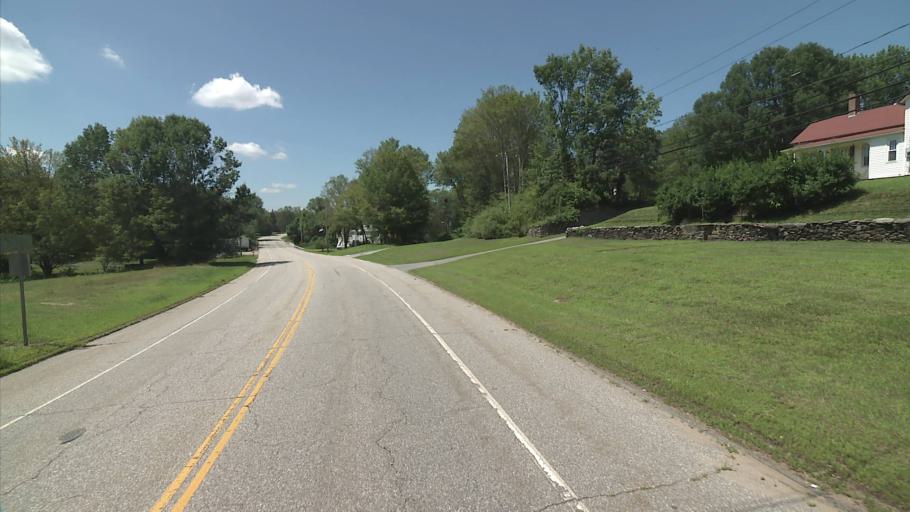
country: US
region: Connecticut
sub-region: Windham County
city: Wauregan
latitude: 41.7216
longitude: -71.9143
